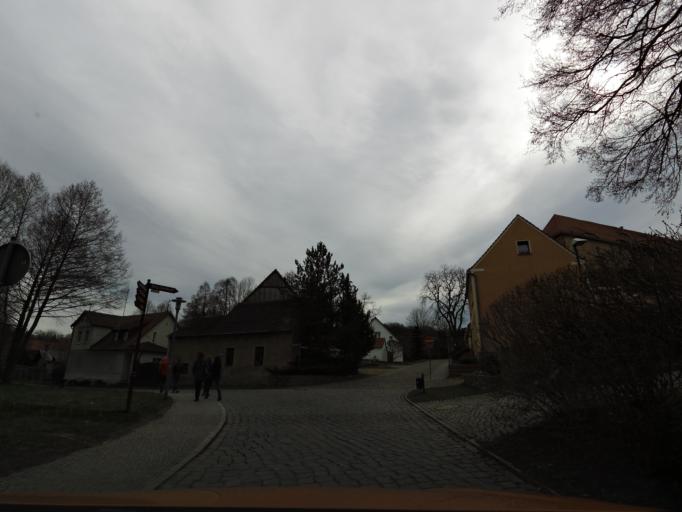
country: DE
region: Brandenburg
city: Belzig
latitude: 52.1383
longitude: 12.5856
